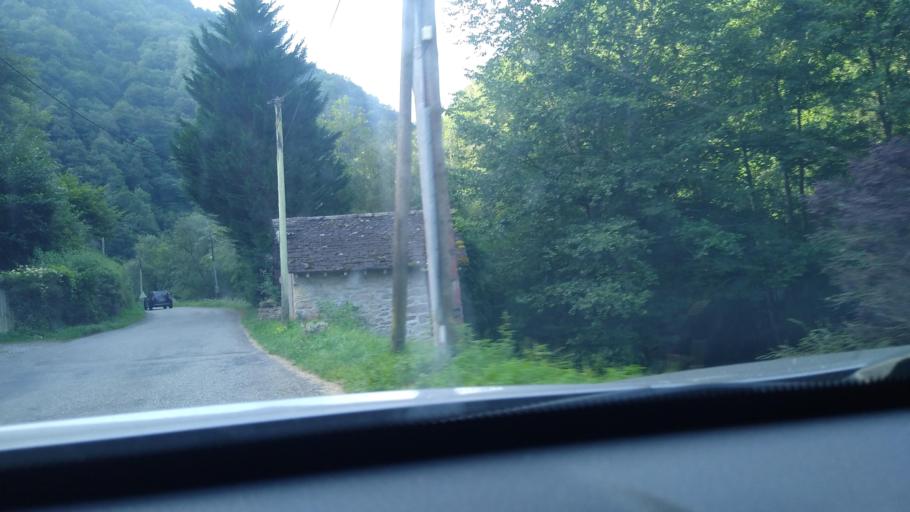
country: FR
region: Midi-Pyrenees
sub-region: Departement de l'Ariege
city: Saint-Girons
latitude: 42.8316
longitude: 1.1985
